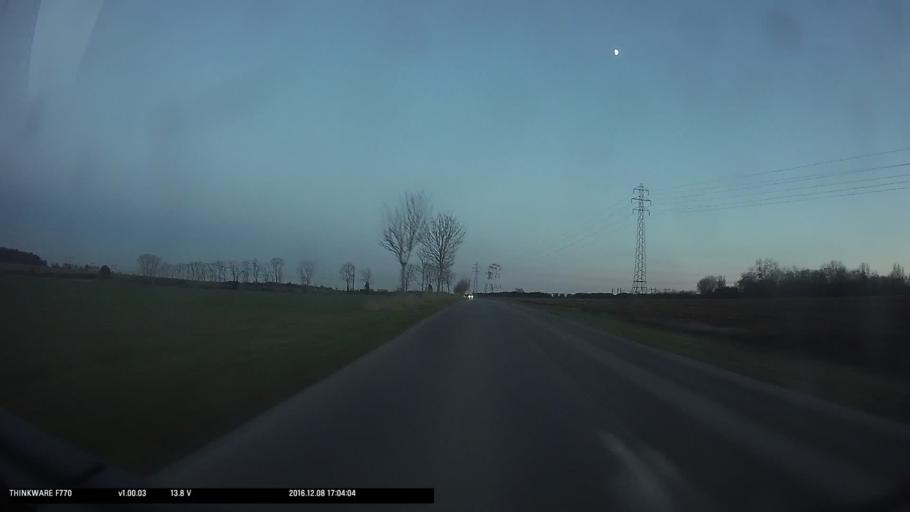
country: FR
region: Ile-de-France
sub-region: Departement du Val-d'Oise
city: Courdimanche
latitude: 49.0607
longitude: 2.0045
